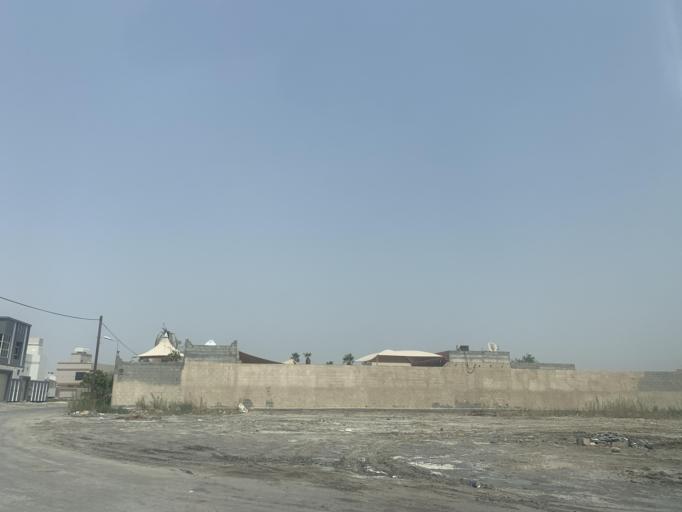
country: BH
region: Central Governorate
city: Madinat Hamad
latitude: 26.1270
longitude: 50.4680
